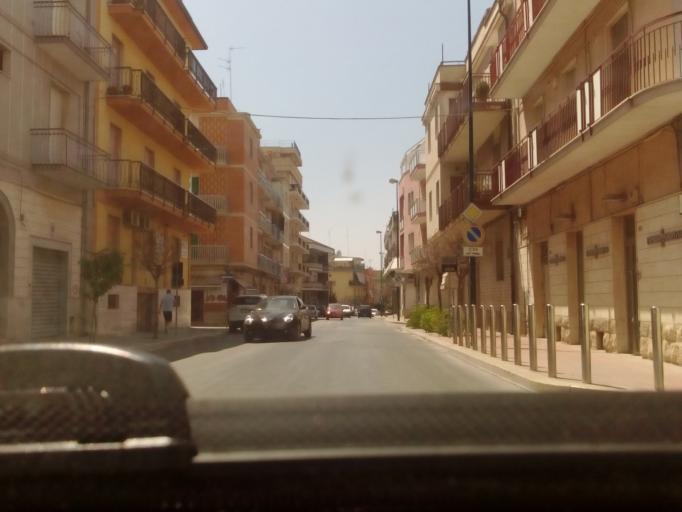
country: IT
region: Apulia
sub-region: Provincia di Bari
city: Gravina in Puglia
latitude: 40.8166
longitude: 16.4240
